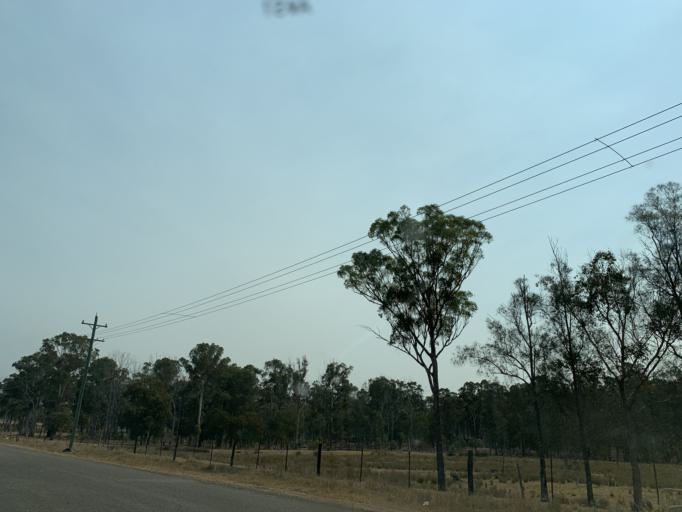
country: AU
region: New South Wales
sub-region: Blacktown
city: Blackett
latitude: -33.7179
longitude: 150.8199
